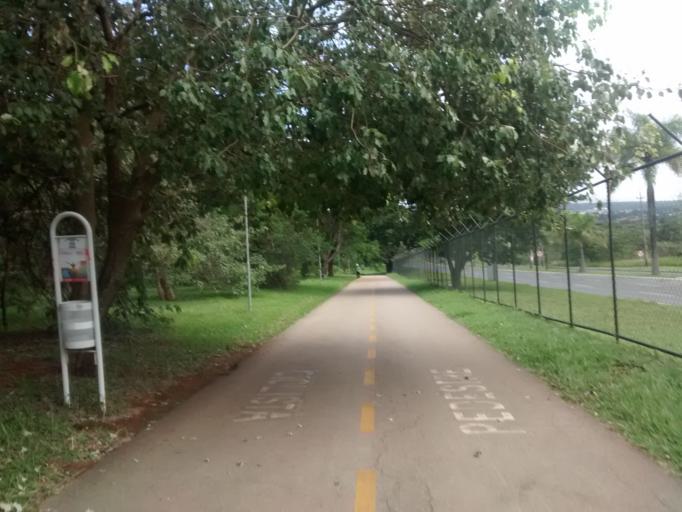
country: BR
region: Federal District
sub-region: Brasilia
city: Brasilia
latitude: -15.7455
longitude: -47.8827
